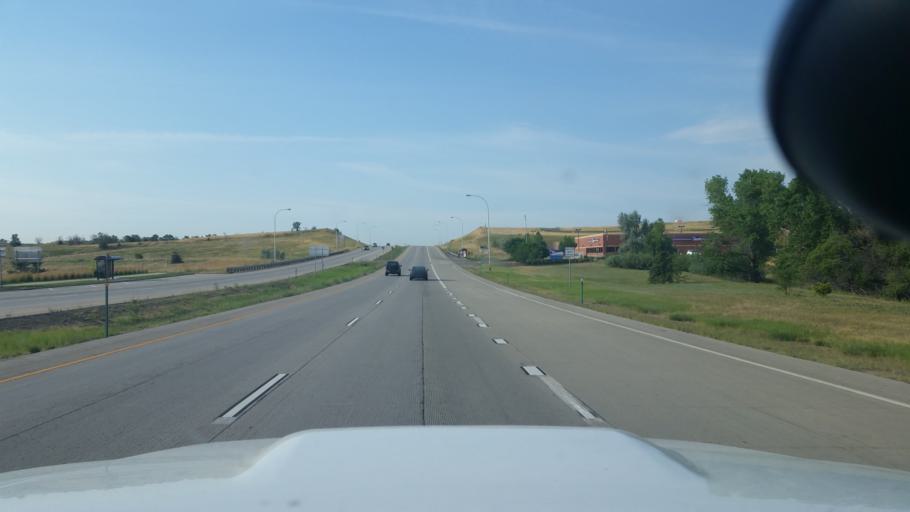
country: US
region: Colorado
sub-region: Broomfield County
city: Broomfield
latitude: 39.9049
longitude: -105.0963
